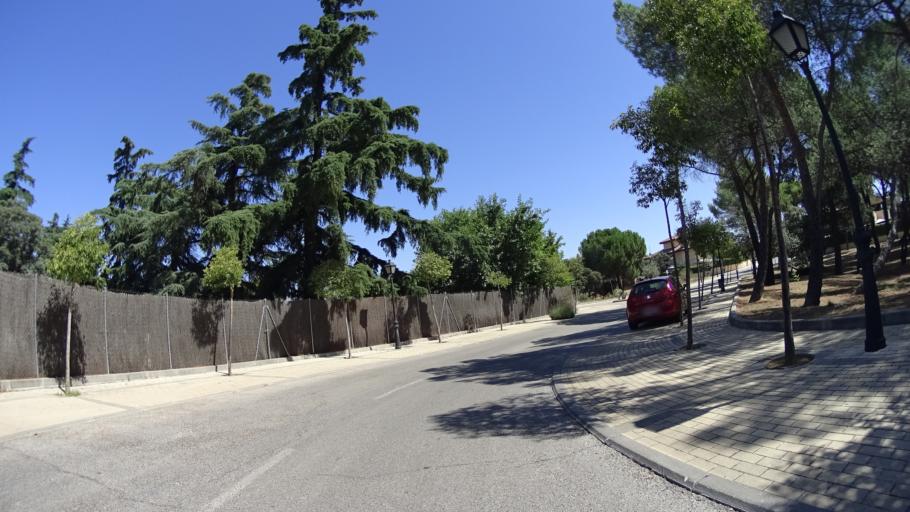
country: ES
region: Madrid
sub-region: Provincia de Madrid
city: Torrelodones
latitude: 40.5720
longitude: -3.9511
